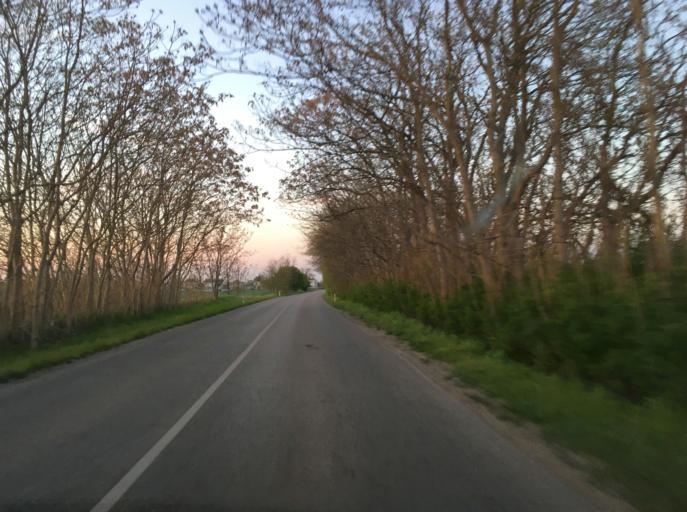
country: SK
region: Nitriansky
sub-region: Okres Nove Zamky
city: Nove Zamky
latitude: 47.9521
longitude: 18.1392
